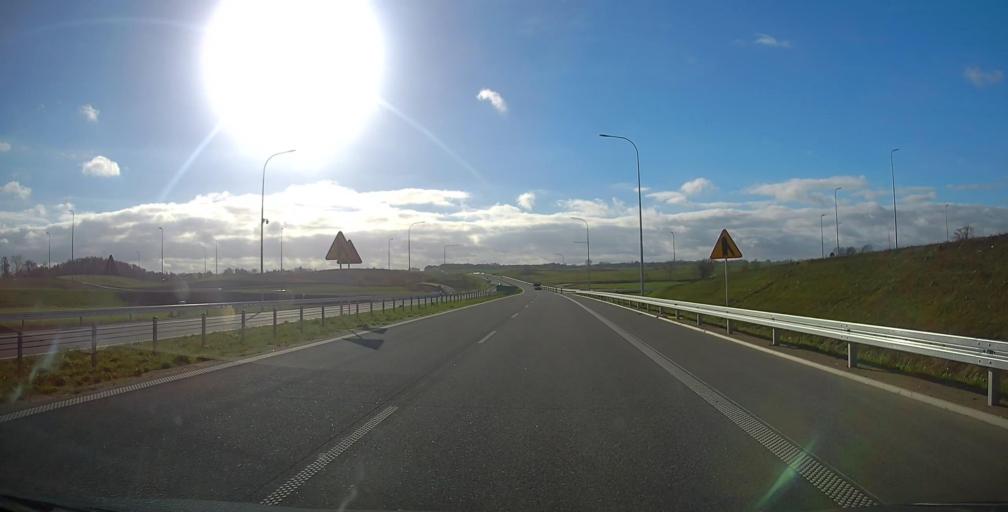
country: PL
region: Warmian-Masurian Voivodeship
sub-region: Powiat elcki
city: Elk
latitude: 53.7428
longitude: 22.2986
